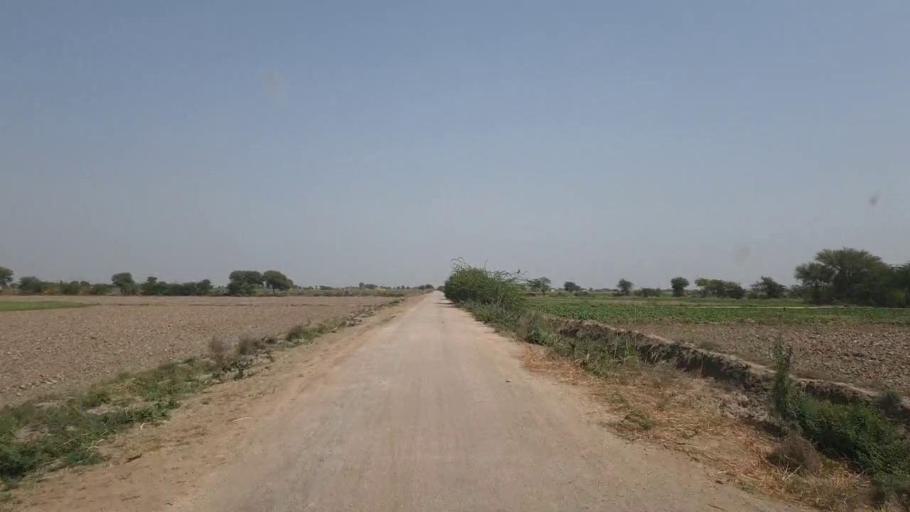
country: PK
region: Sindh
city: Jati
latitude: 24.4774
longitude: 68.5541
